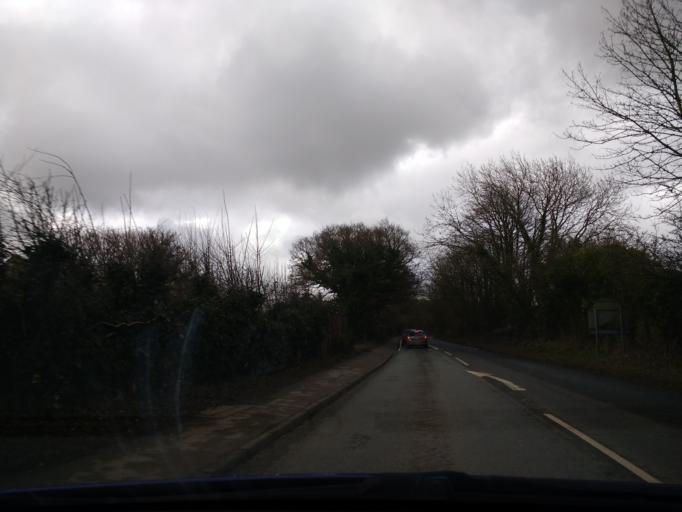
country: GB
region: England
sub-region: Cumbria
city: Maryport
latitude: 54.7101
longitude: -3.4733
